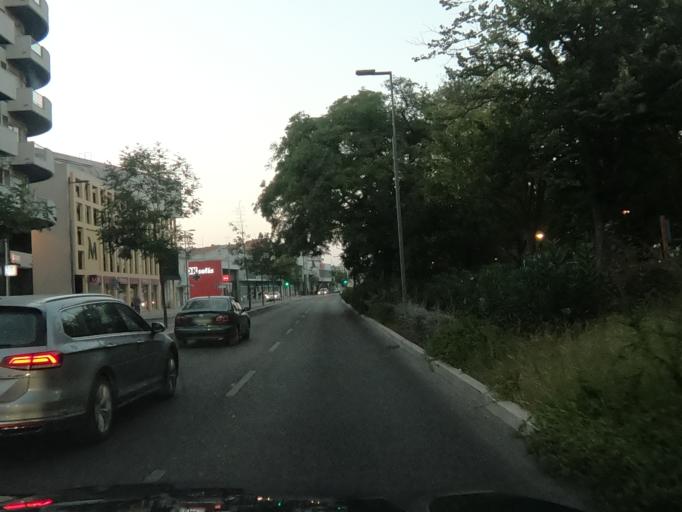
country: PT
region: Santarem
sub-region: Santarem
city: Santarem
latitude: 39.2351
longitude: -8.6869
